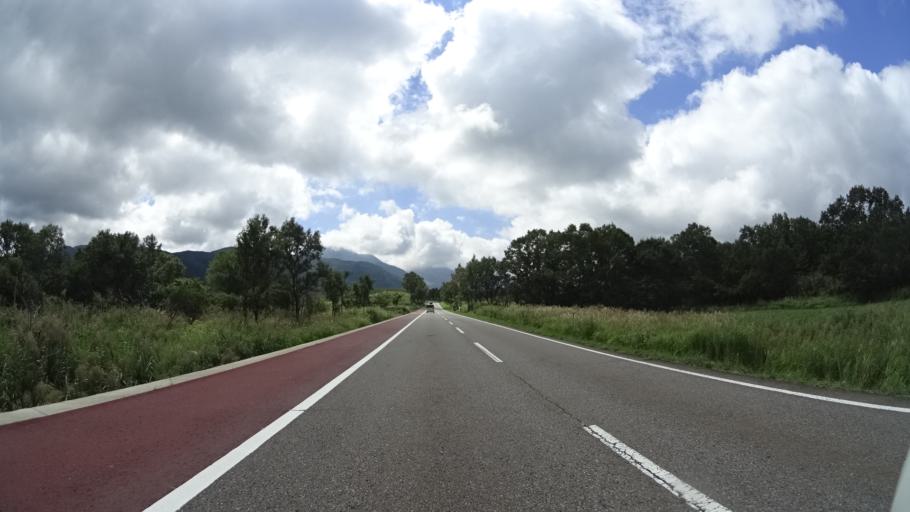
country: JP
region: Oita
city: Tsukawaki
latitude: 33.1494
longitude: 131.2404
